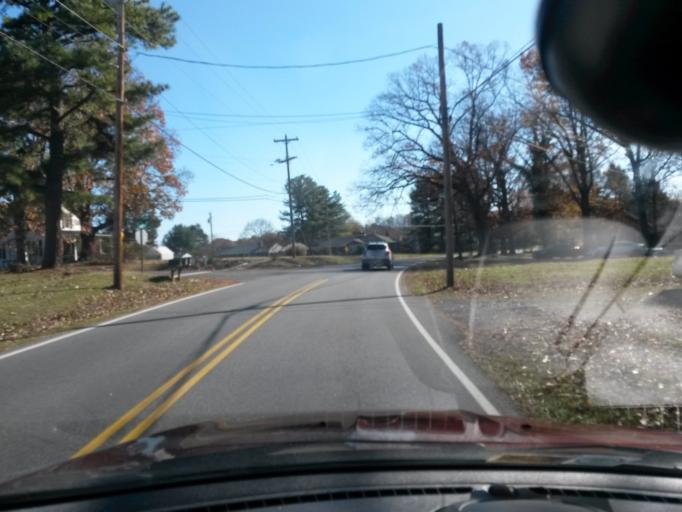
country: US
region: Virginia
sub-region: City of Bedford
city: Bedford
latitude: 37.3512
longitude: -79.5279
